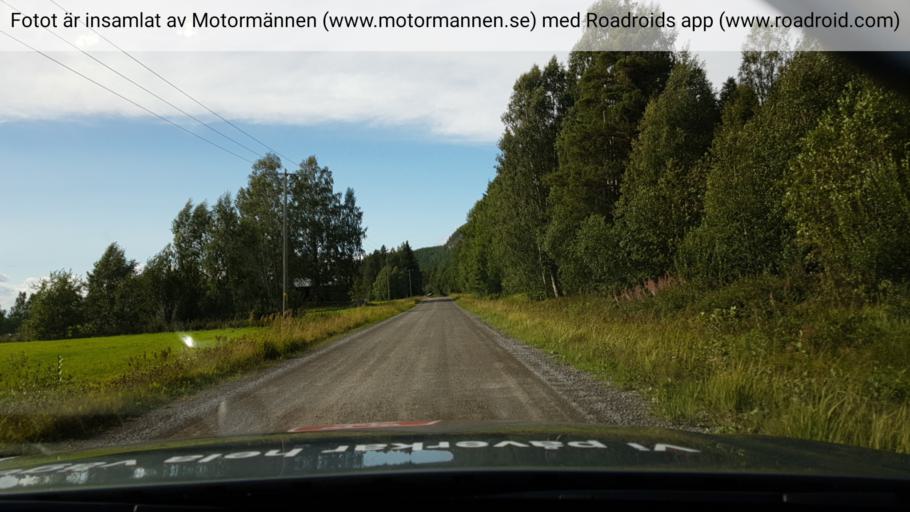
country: SE
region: Jaemtland
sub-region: Braecke Kommun
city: Braecke
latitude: 63.2045
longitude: 15.4095
